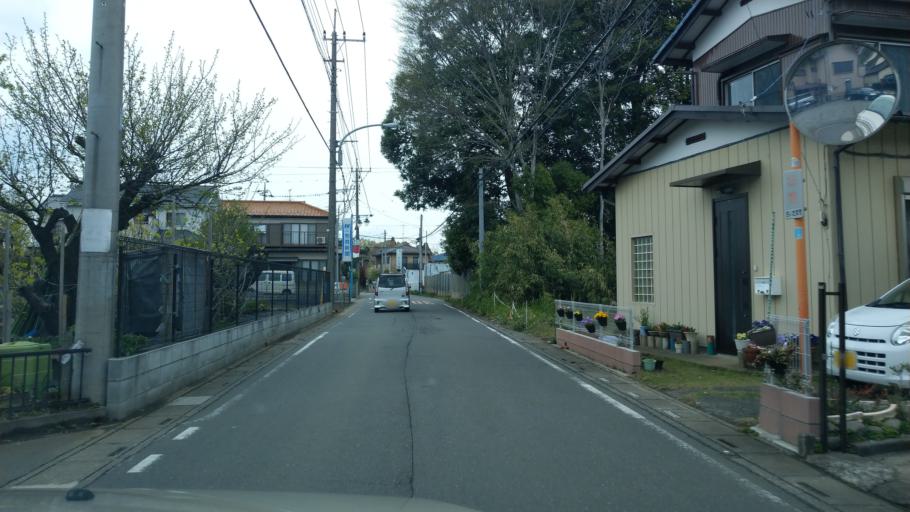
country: JP
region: Saitama
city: Ageoshimo
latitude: 35.9376
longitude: 139.5844
